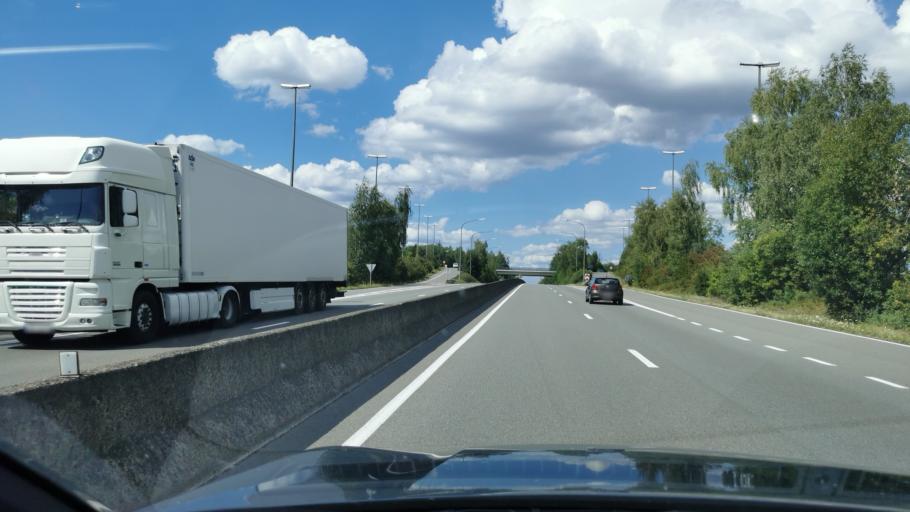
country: BE
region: Wallonia
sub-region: Province du Luxembourg
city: Messancy
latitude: 49.5844
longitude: 5.8089
